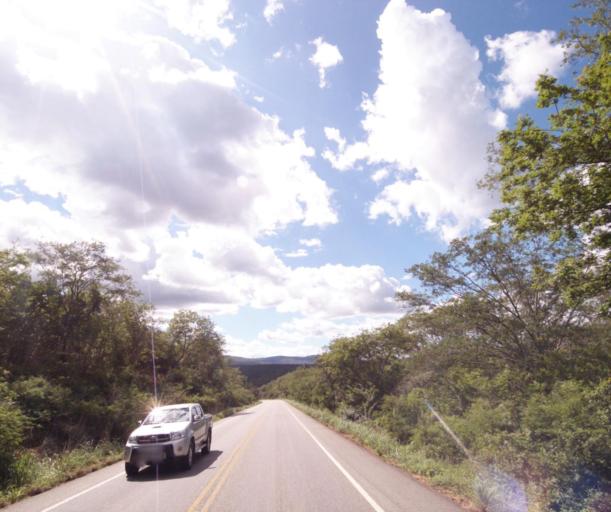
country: BR
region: Bahia
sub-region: Caetite
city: Caetite
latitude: -14.1298
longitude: -42.3982
